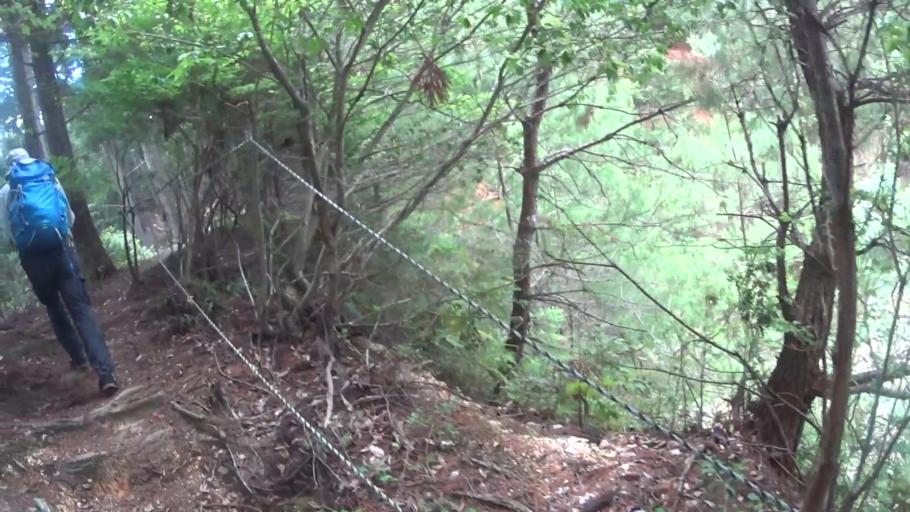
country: JP
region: Nara
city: Yoshino-cho
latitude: 34.3628
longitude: 135.8707
